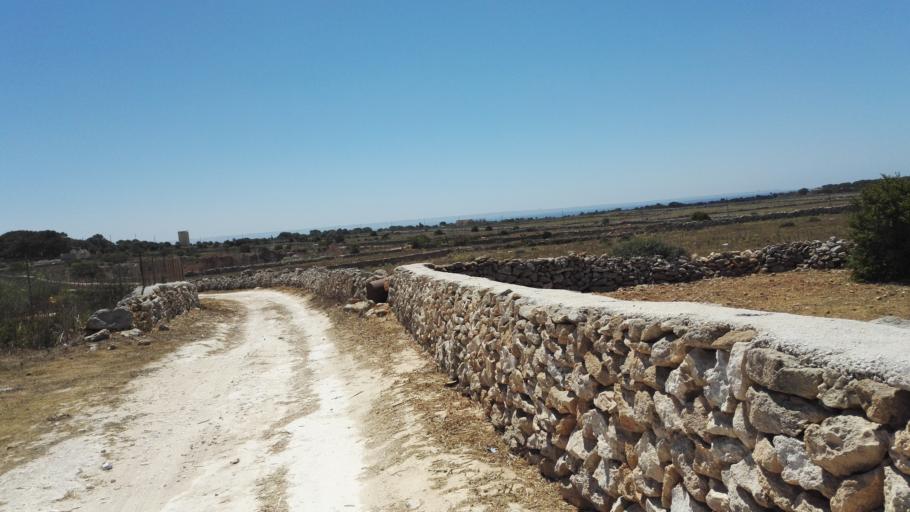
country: IT
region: Sicily
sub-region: Trapani
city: Favignana
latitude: 37.9192
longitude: 12.3595
